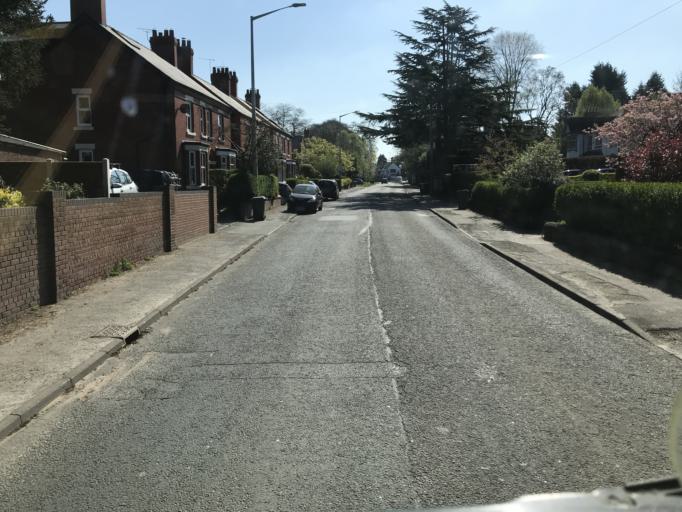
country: GB
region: England
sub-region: Cheshire East
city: Middlewich
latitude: 53.1956
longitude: -2.4565
